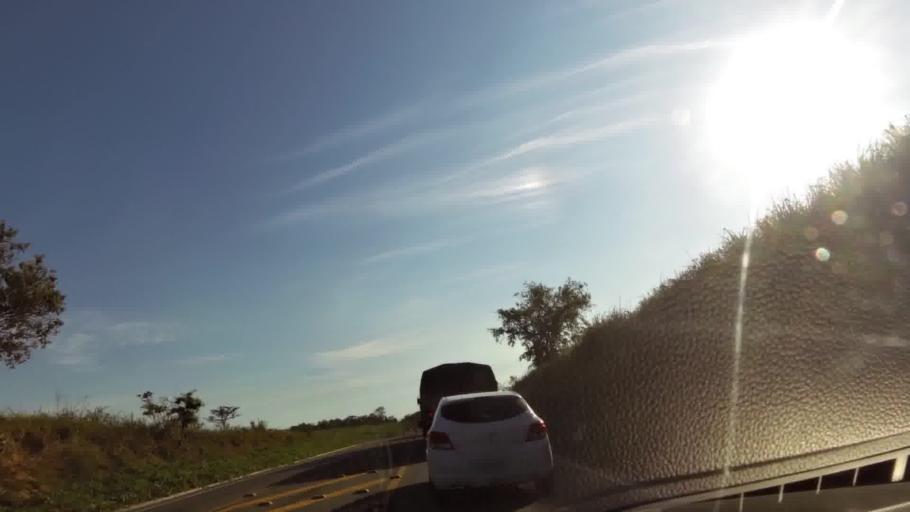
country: BR
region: Espirito Santo
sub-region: Viana
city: Viana
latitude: -20.4741
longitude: -40.4705
